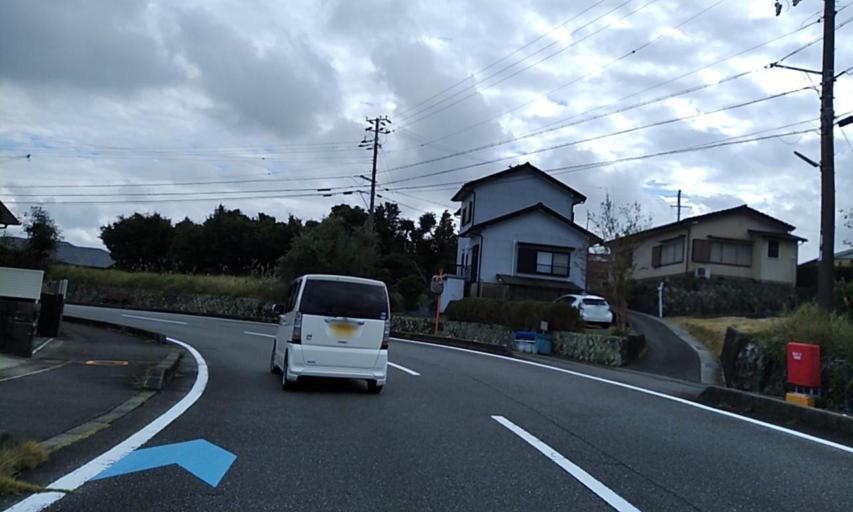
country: JP
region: Wakayama
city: Shingu
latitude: 33.5859
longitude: 135.9478
